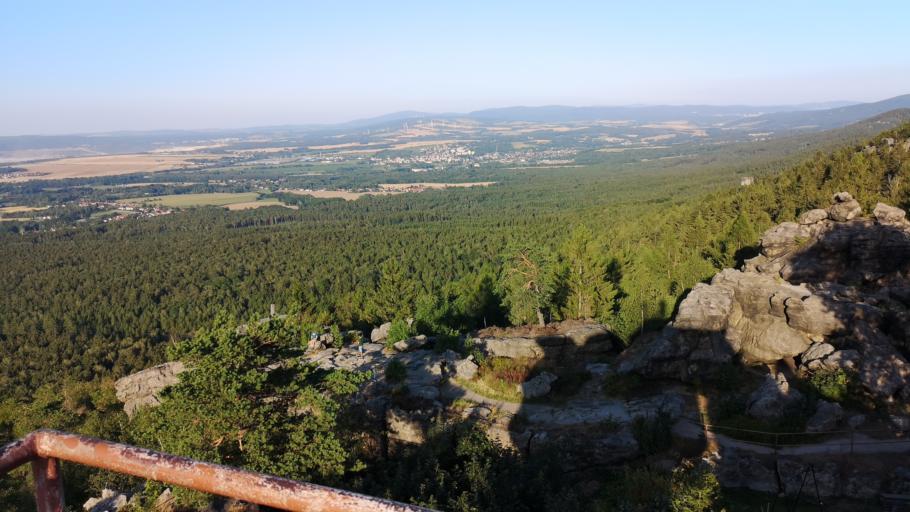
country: DE
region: Saxony
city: Kurort Oybin
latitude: 50.8494
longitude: 14.7615
